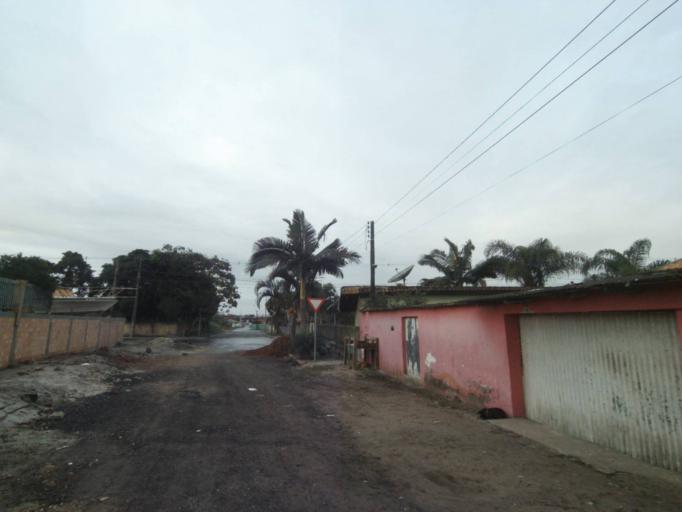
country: BR
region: Parana
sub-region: Paranagua
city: Paranagua
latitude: -25.5738
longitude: -48.5722
